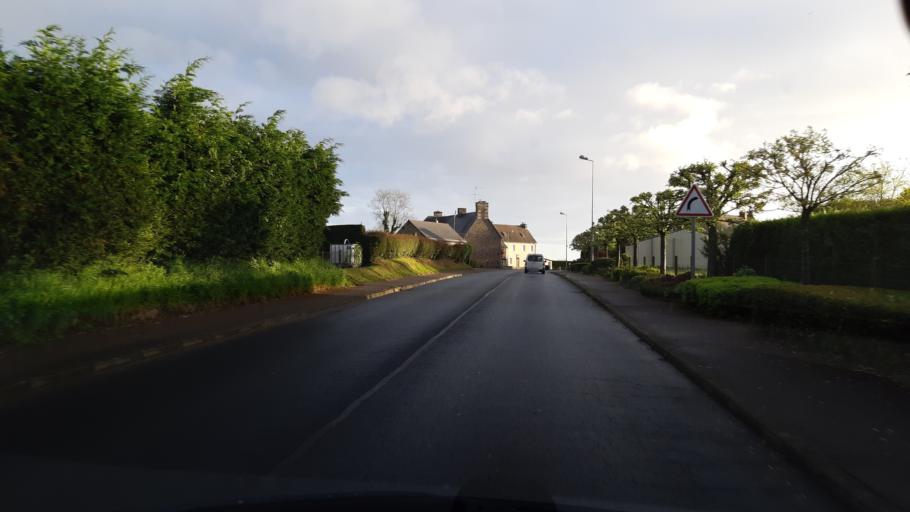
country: FR
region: Lower Normandy
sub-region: Departement de la Manche
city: Tessy-sur-Vire
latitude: 49.0267
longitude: -1.1450
